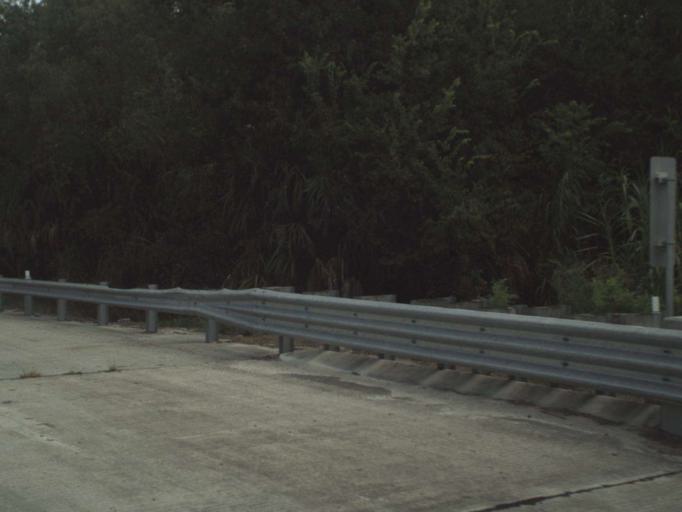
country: US
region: Florida
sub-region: Martin County
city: Indiantown
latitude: 27.0119
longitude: -80.6265
